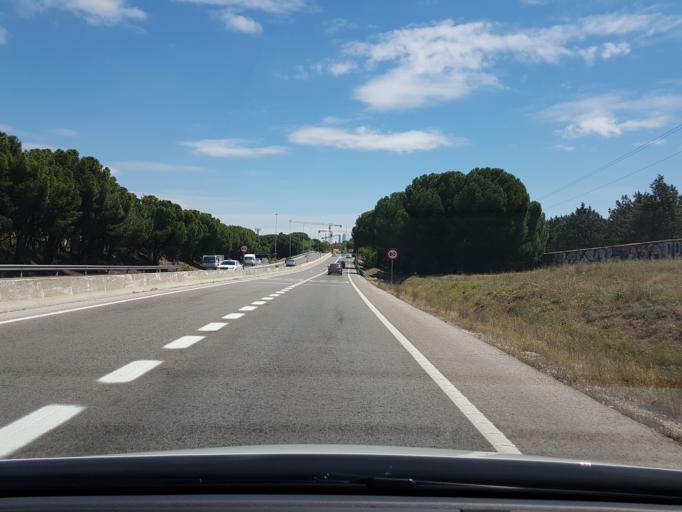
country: ES
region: Madrid
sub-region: Provincia de Madrid
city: Moncloa-Aravaca
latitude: 40.4483
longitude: -3.7657
